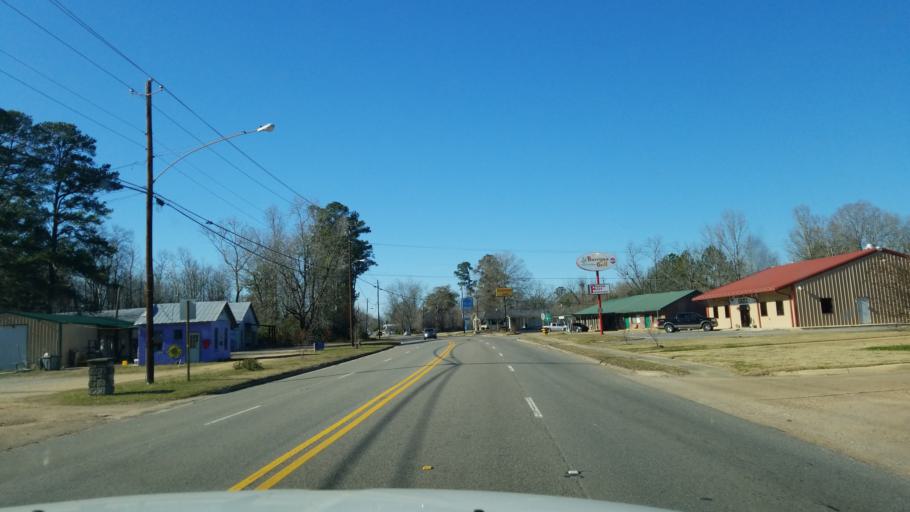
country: US
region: Alabama
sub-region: Pickens County
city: Reform
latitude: 33.3773
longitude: -88.0109
